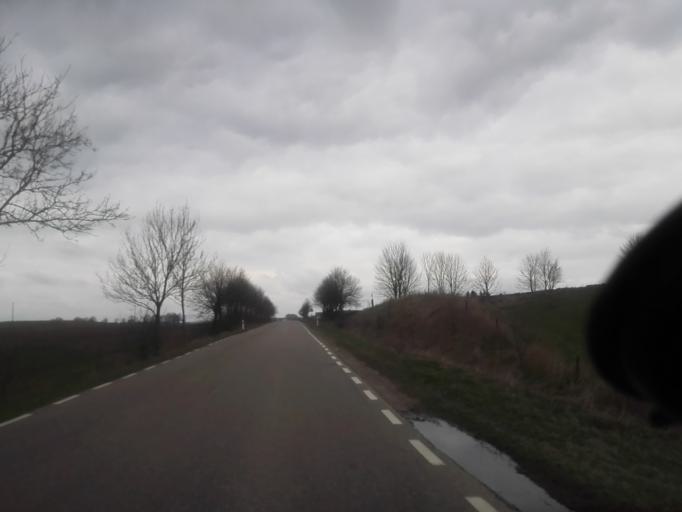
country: PL
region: Podlasie
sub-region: Suwalki
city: Suwalki
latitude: 54.2202
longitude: 22.9118
